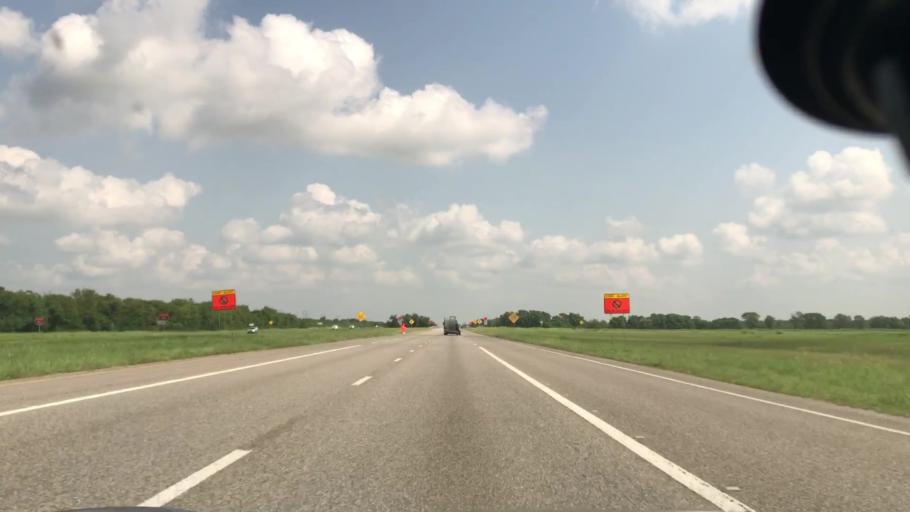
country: US
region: Texas
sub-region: Brazoria County
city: Rosharon
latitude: 29.3820
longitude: -95.4266
